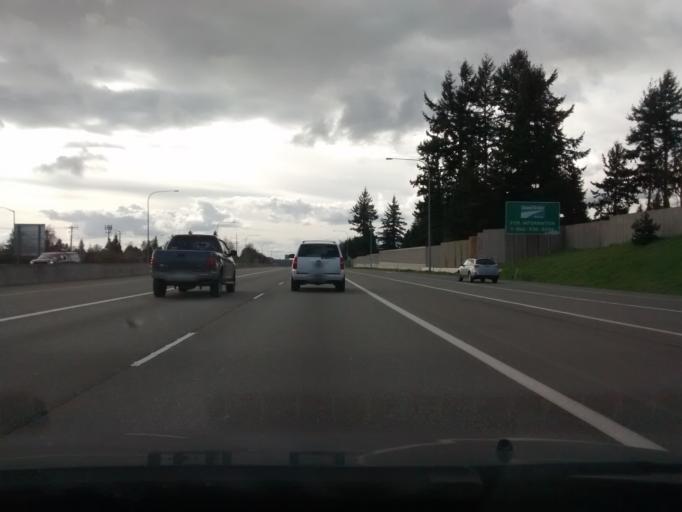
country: US
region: Washington
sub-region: Pierce County
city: Fircrest
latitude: 47.2582
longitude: -122.5200
